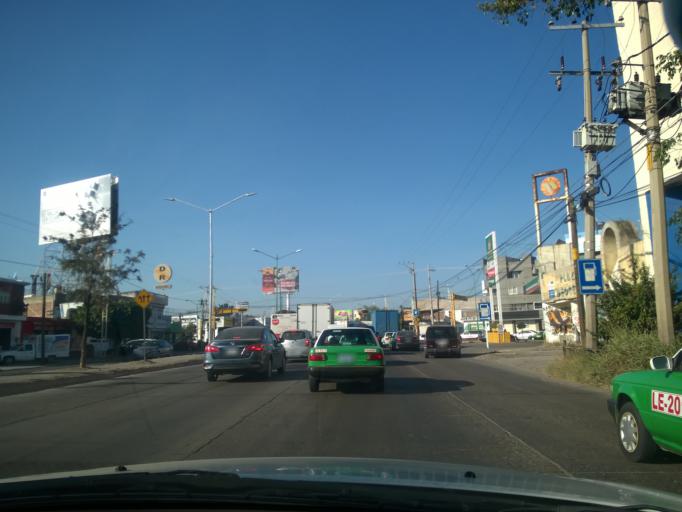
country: MX
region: Guanajuato
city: Leon
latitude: 21.0976
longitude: -101.6462
